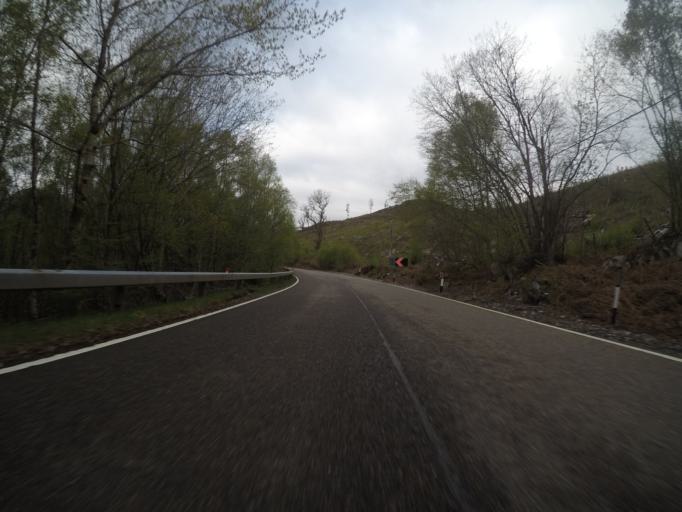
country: GB
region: Scotland
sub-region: Highland
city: Kingussie
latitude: 56.9610
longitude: -4.4590
